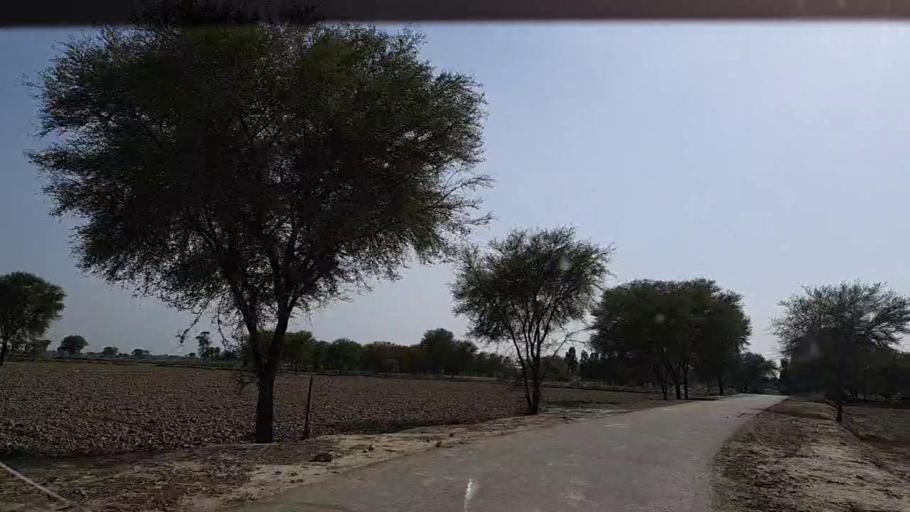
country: PK
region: Sindh
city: Phulji
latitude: 26.9260
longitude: 67.6830
